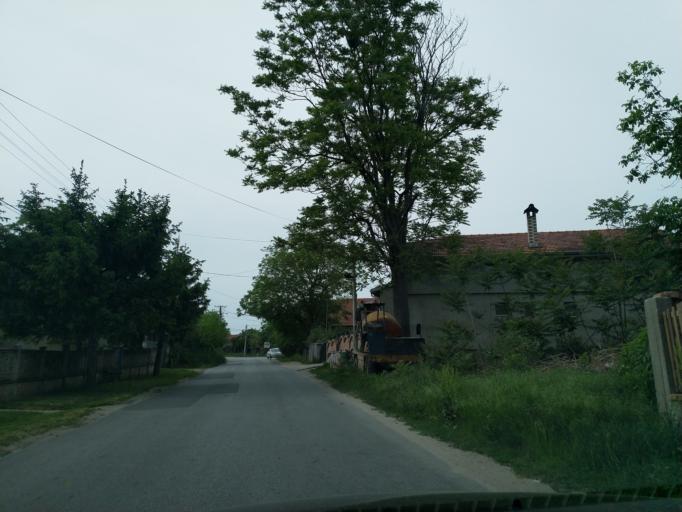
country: RS
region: Central Serbia
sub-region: Pomoravski Okrug
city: Jagodina
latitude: 43.9686
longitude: 21.2276
